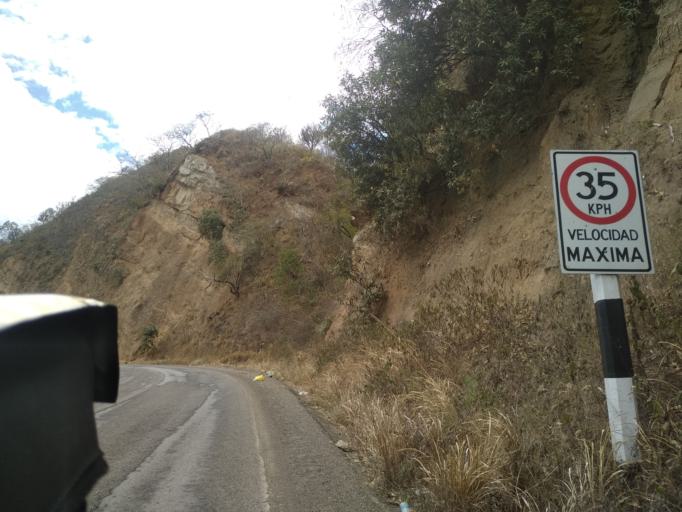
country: PE
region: Cajamarca
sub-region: Provincia de San Ignacio
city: La Coipa
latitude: -5.3718
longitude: -78.7797
